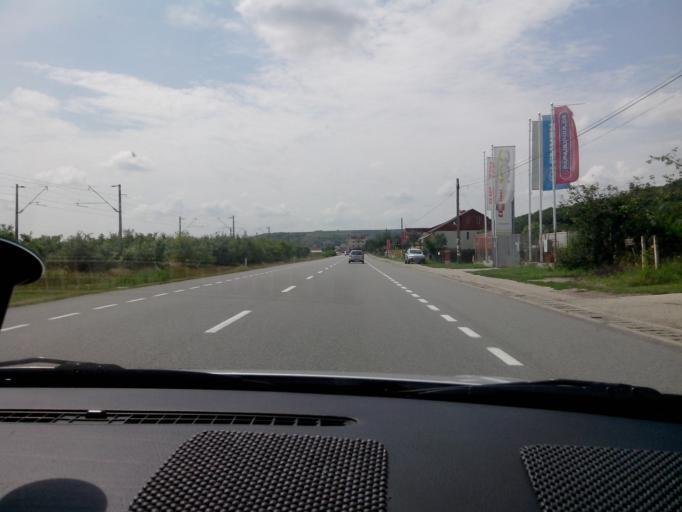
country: RO
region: Cluj
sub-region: Comuna Apahida
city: Apahida
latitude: 46.8413
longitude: 23.7491
